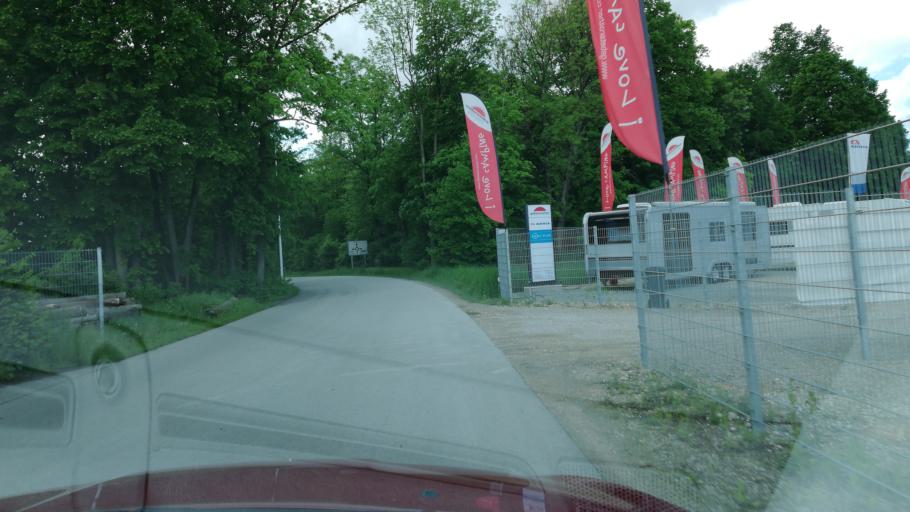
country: AT
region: Upper Austria
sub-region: Wels-Land
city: Marchtrenk
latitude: 48.1738
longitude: 14.1261
